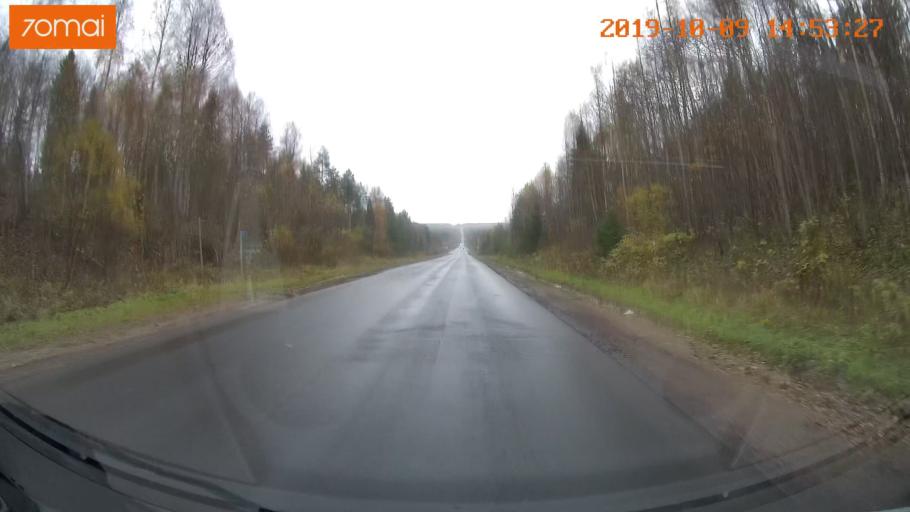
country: RU
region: Kostroma
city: Chistyye Bory
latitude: 58.3675
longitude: 41.6384
